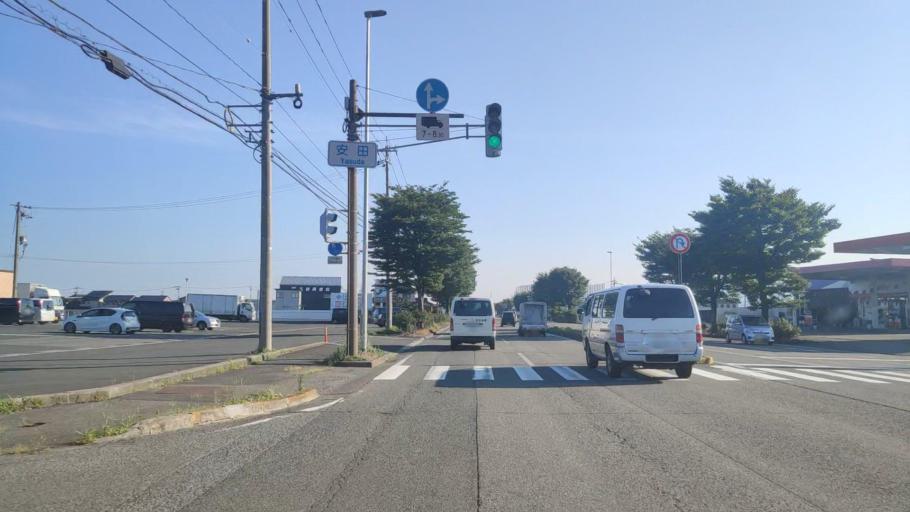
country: JP
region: Fukui
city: Maruoka
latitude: 36.1239
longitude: 136.2595
